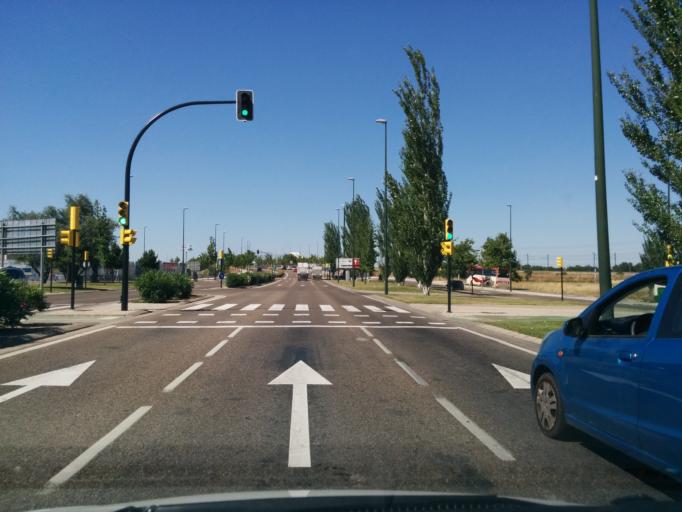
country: ES
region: Aragon
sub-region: Provincia de Zaragoza
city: Zaragoza
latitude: 41.6443
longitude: -0.8571
